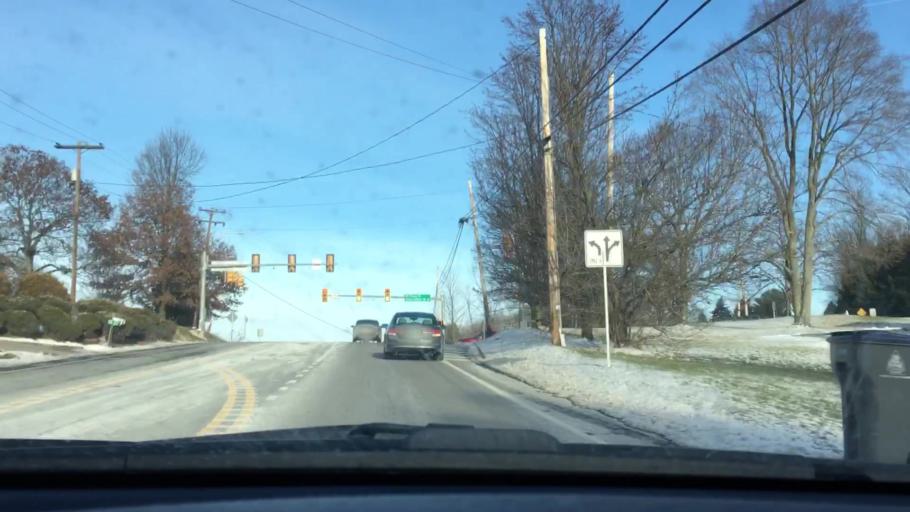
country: US
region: Pennsylvania
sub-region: Washington County
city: Thompsonville
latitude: 40.2725
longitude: -80.1092
